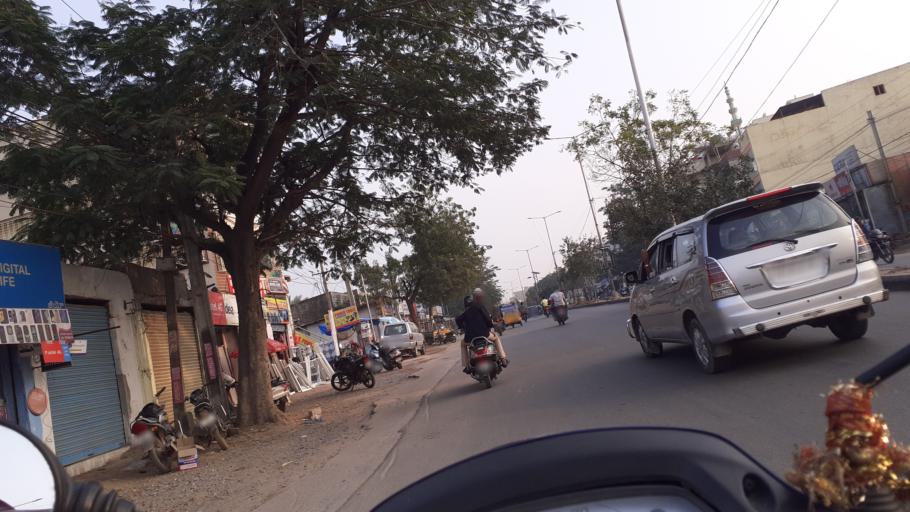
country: IN
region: Telangana
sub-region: Rangareddi
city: Kukatpalli
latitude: 17.4791
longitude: 78.3615
